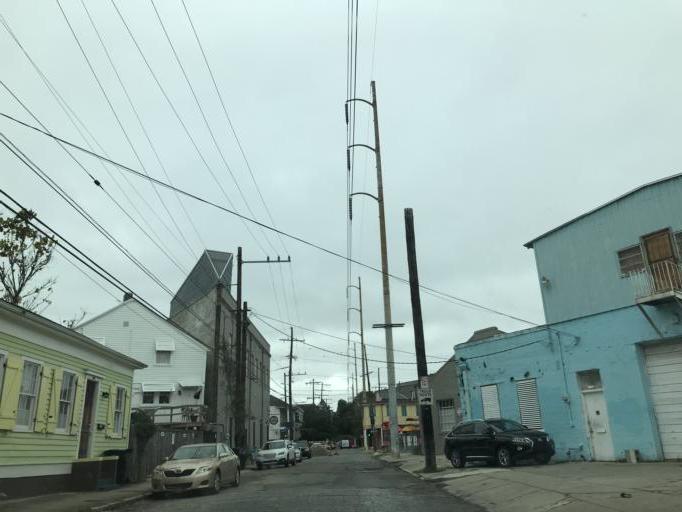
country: US
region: Louisiana
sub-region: Orleans Parish
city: New Orleans
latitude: 29.9317
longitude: -90.0725
